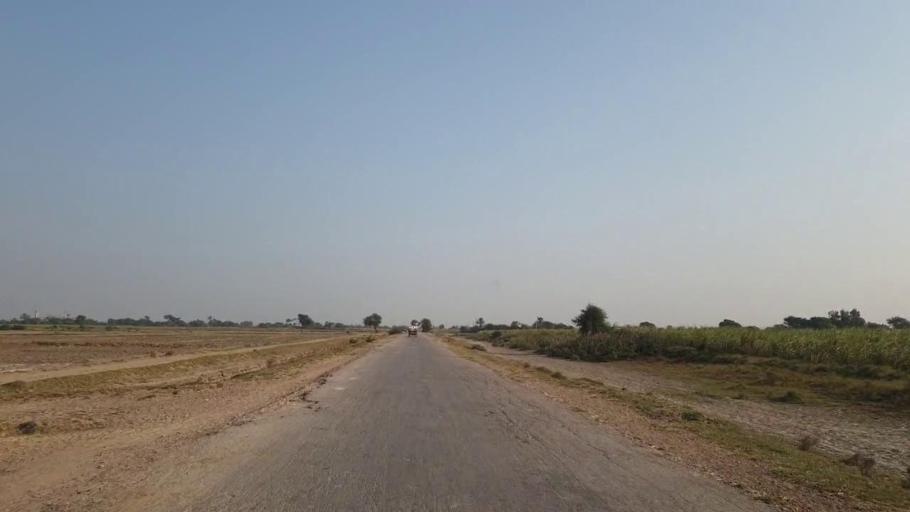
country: PK
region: Sindh
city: Bulri
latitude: 24.9738
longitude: 68.4012
